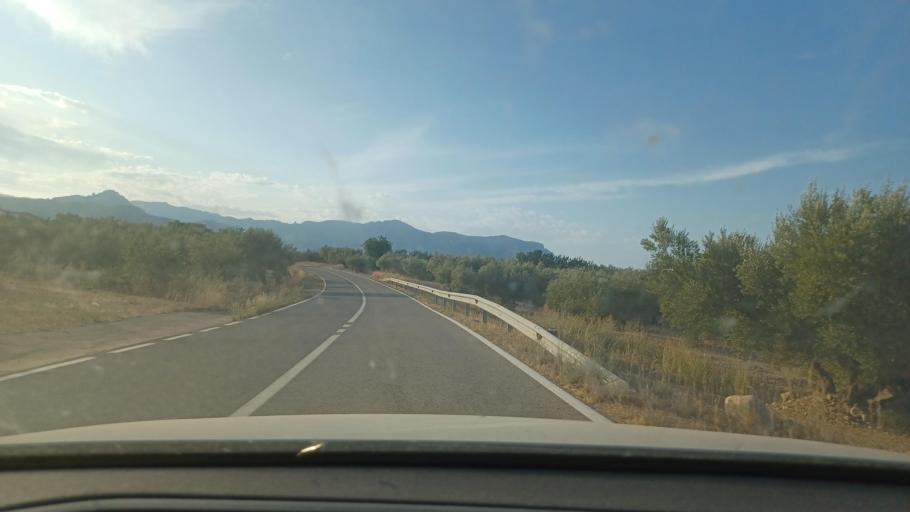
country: ES
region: Catalonia
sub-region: Provincia de Tarragona
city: Mas de Barberans
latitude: 40.7164
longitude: 0.4023
